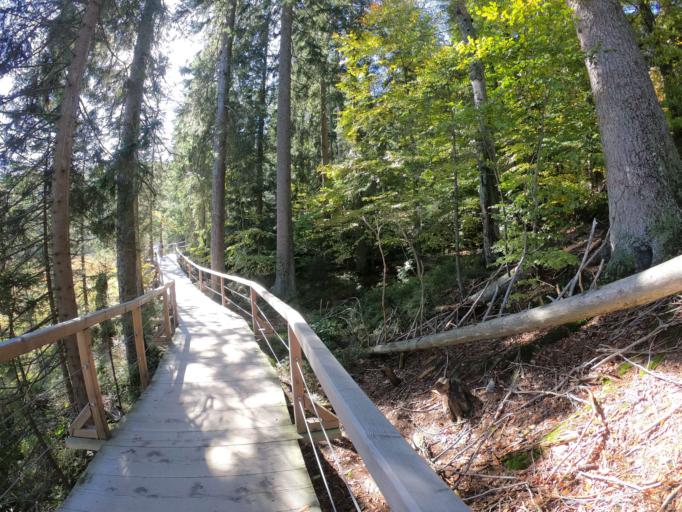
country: DE
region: Bavaria
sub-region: Lower Bavaria
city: Bayerisch Eisenstein
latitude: 49.0986
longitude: 13.1507
